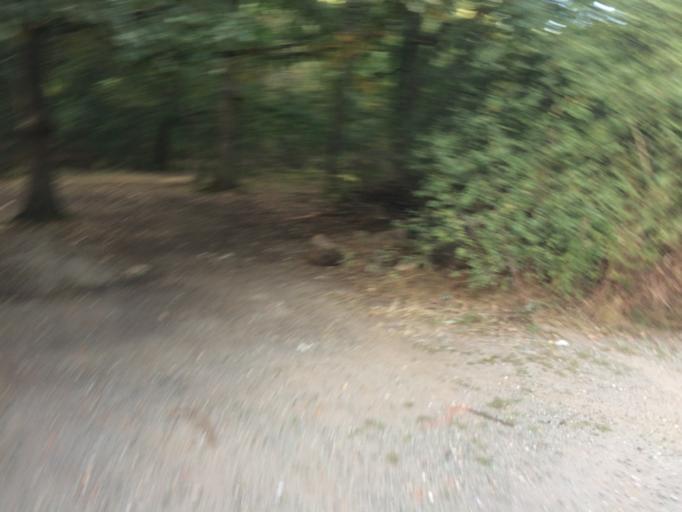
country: FR
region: Ile-de-France
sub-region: Departement de l'Essonne
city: Igny
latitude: 48.7395
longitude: 2.2156
